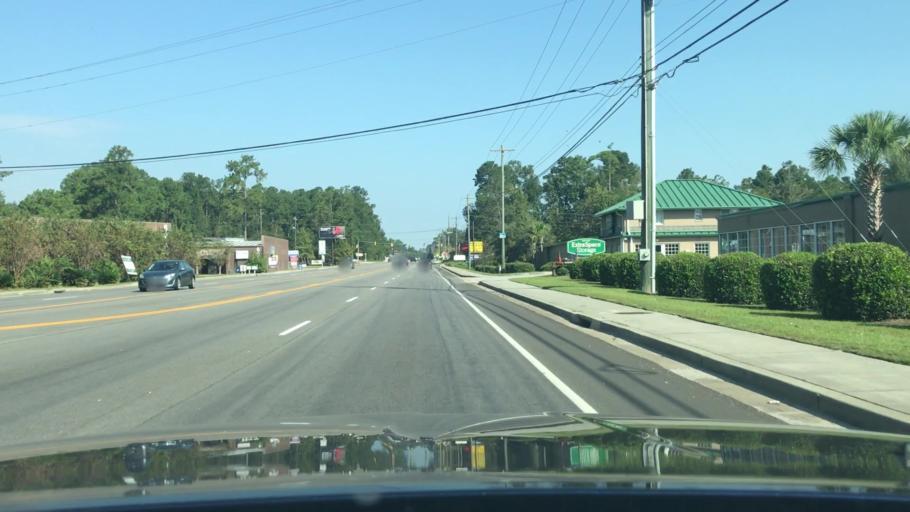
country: US
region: South Carolina
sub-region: Dorchester County
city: Centerville
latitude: 32.9808
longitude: -80.1745
